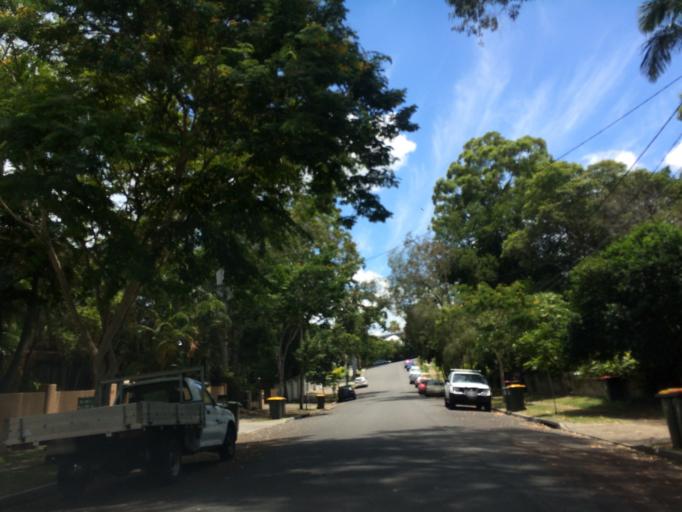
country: AU
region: Queensland
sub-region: Brisbane
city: South Brisbane
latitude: -27.4893
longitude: 153.0120
